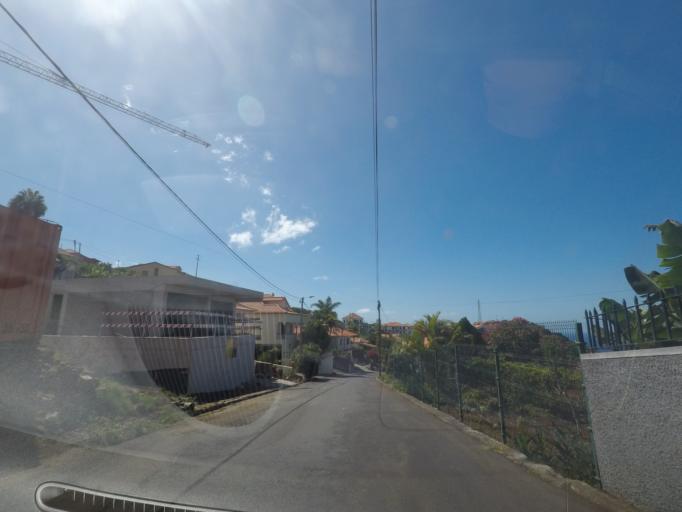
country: PT
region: Madeira
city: Ponta do Sol
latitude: 32.6890
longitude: -17.0909
